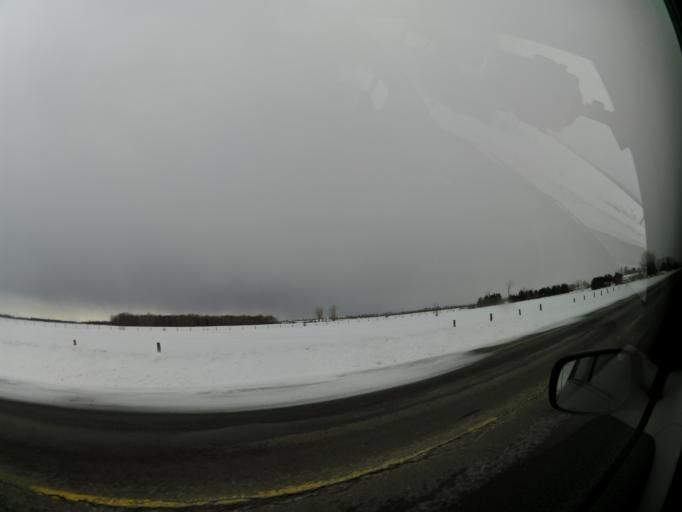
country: CA
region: Ontario
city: Clarence-Rockland
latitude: 45.4507
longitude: -75.4432
